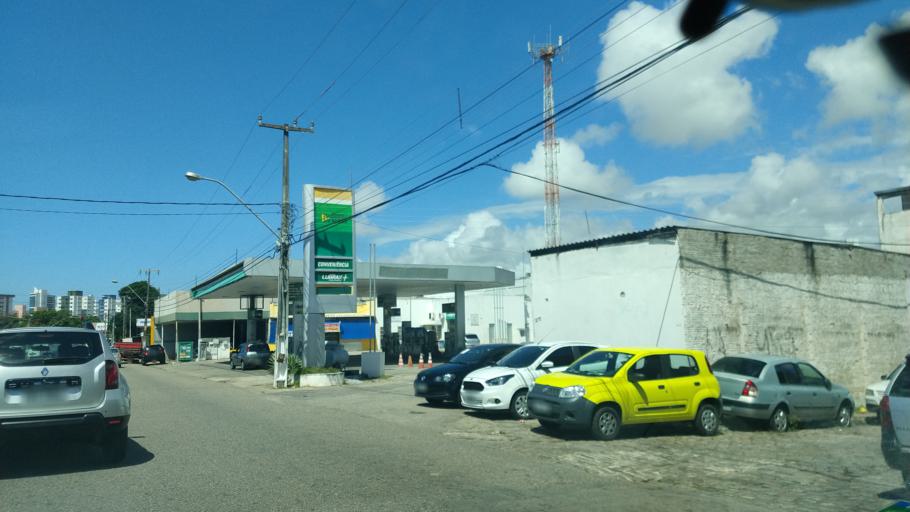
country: BR
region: Rio Grande do Norte
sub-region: Natal
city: Natal
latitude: -5.8085
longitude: -35.2120
